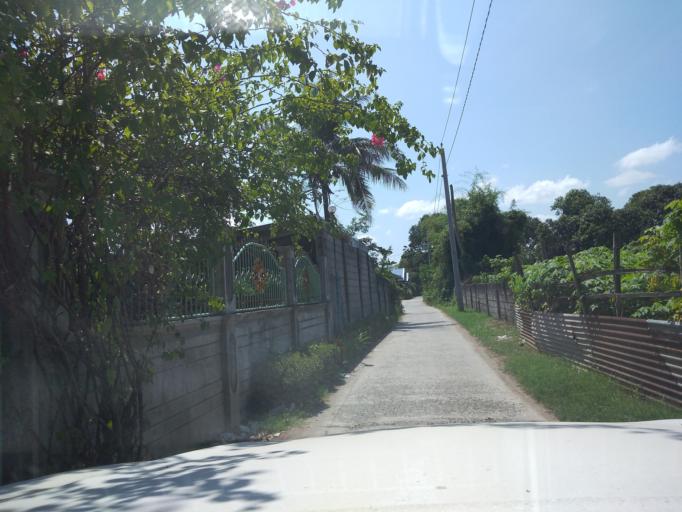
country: PH
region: Central Luzon
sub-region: Province of Pampanga
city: Lourdes
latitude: 15.0183
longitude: 120.8528
